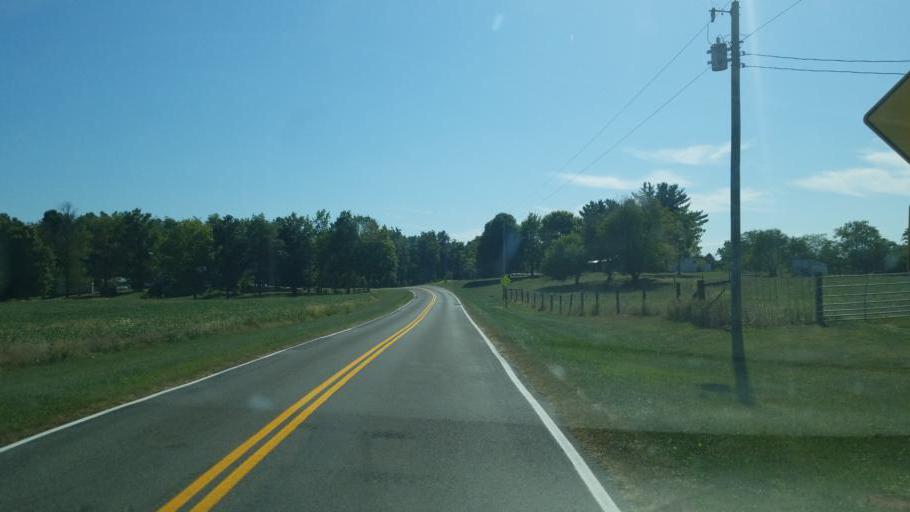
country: US
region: Ohio
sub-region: Champaign County
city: North Lewisburg
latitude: 40.1500
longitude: -83.6007
